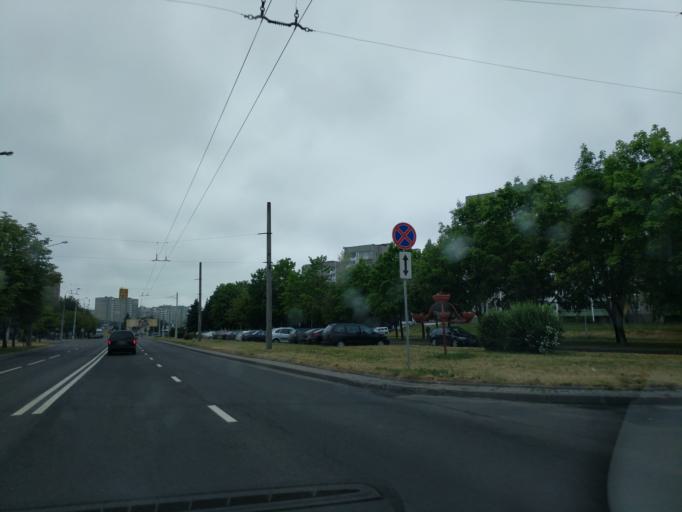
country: BY
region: Minsk
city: Novoye Medvezhino
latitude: 53.8642
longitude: 27.4678
